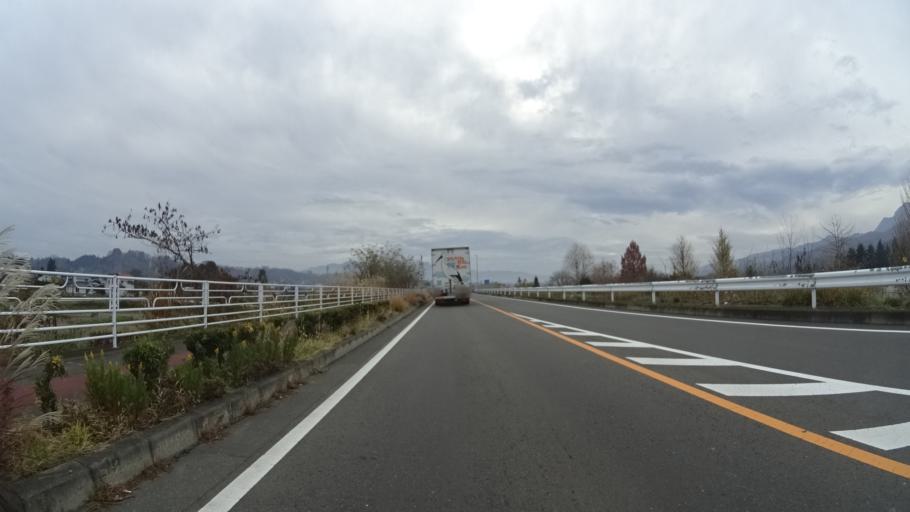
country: JP
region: Gunma
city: Numata
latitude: 36.6492
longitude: 139.0251
